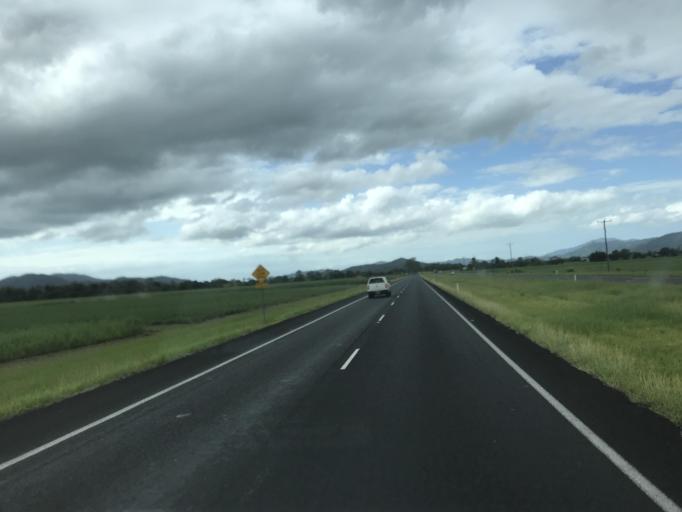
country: AU
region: Queensland
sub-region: Cassowary Coast
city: Innisfail
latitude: -17.7726
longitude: 146.0283
